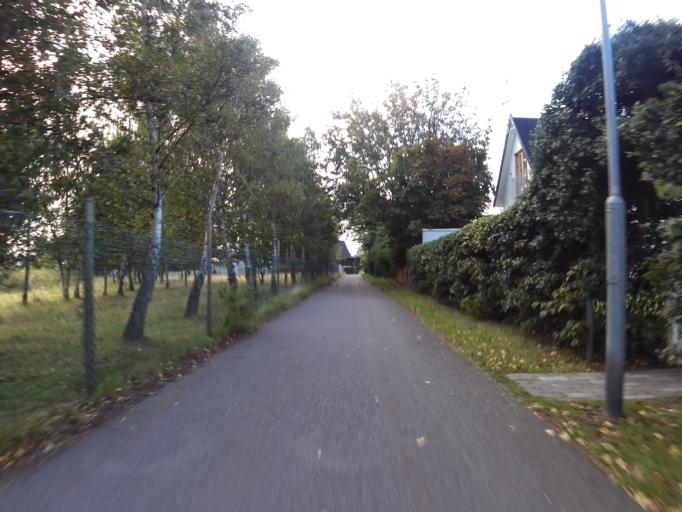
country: SE
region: Skane
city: Bjarred
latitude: 55.7028
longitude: 13.0439
